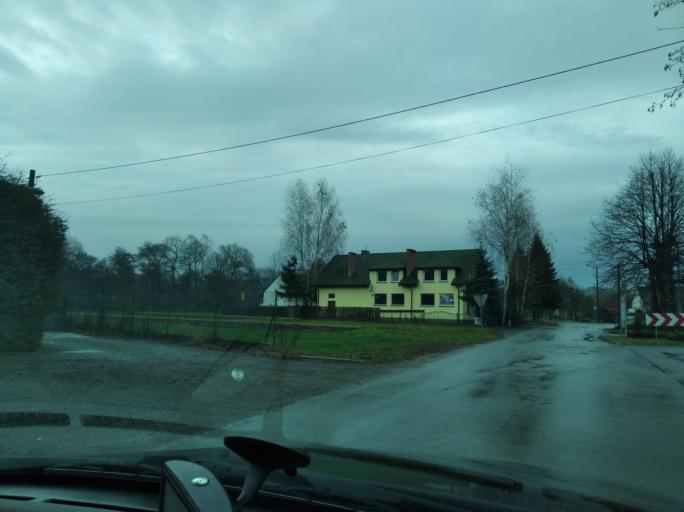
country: PL
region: Subcarpathian Voivodeship
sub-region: Powiat rzeszowski
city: Lubenia
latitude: 49.9236
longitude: 21.9491
